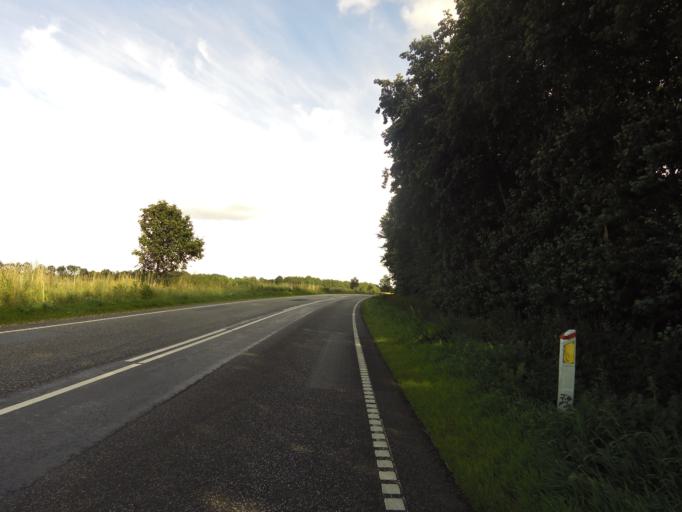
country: DK
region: South Denmark
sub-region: Tonder Kommune
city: Toftlund
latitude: 55.2166
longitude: 9.0294
